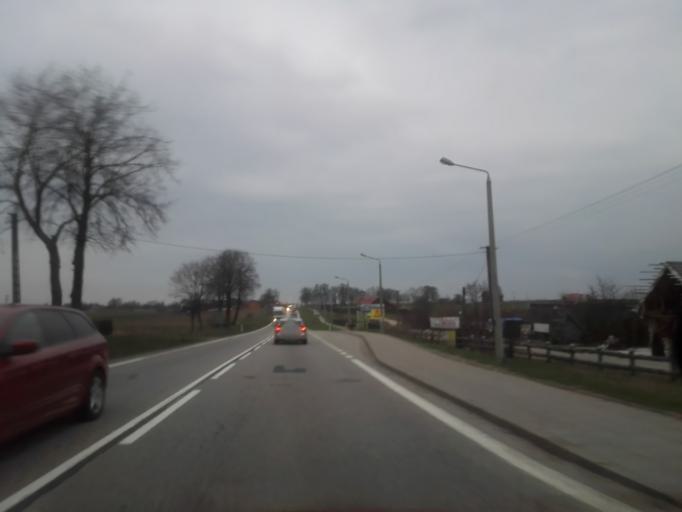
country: PL
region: Podlasie
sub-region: Powiat lomzynski
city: Piatnica
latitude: 53.2518
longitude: 22.1209
